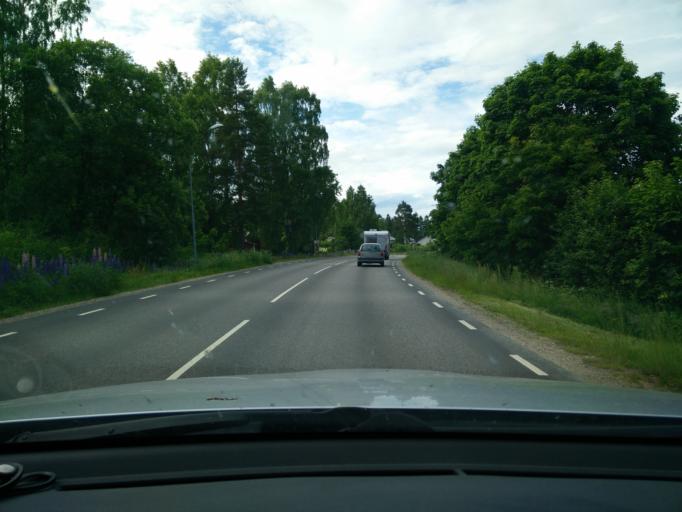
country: SE
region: Gaevleborg
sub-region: Nordanstigs Kommun
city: Bergsjoe
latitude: 61.9726
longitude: 17.0538
